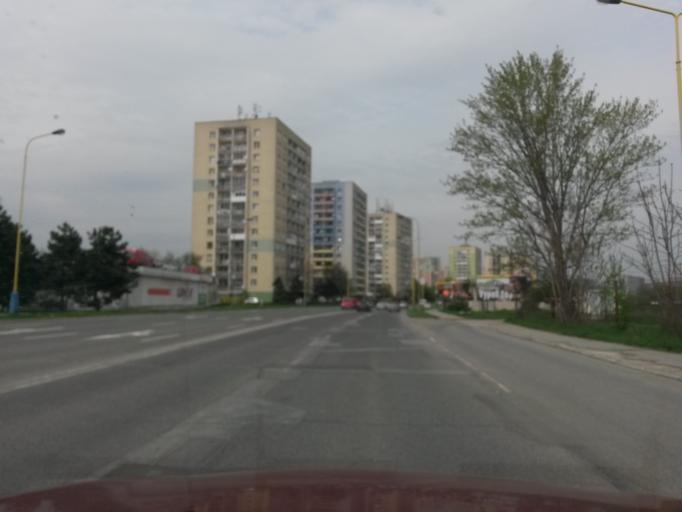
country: SK
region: Kosicky
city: Kosice
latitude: 48.7097
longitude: 21.2653
